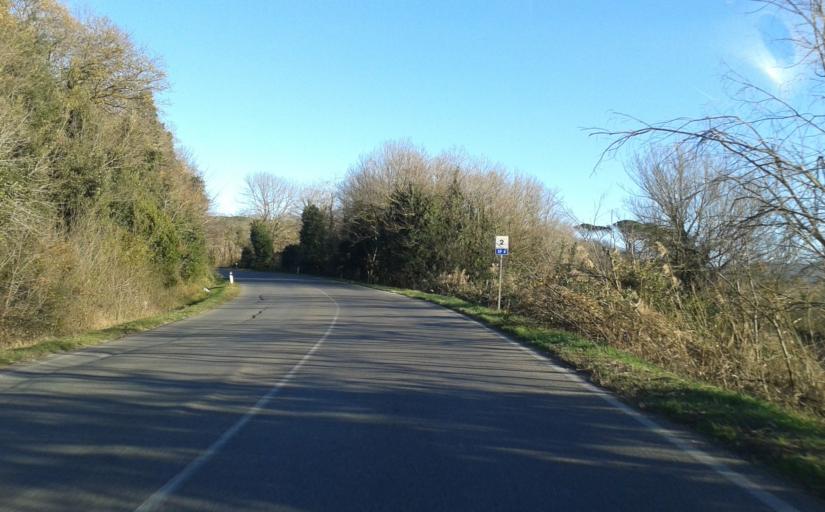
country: IT
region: Tuscany
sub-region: Provincia di Livorno
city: Livorno
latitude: 43.5688
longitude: 10.3587
